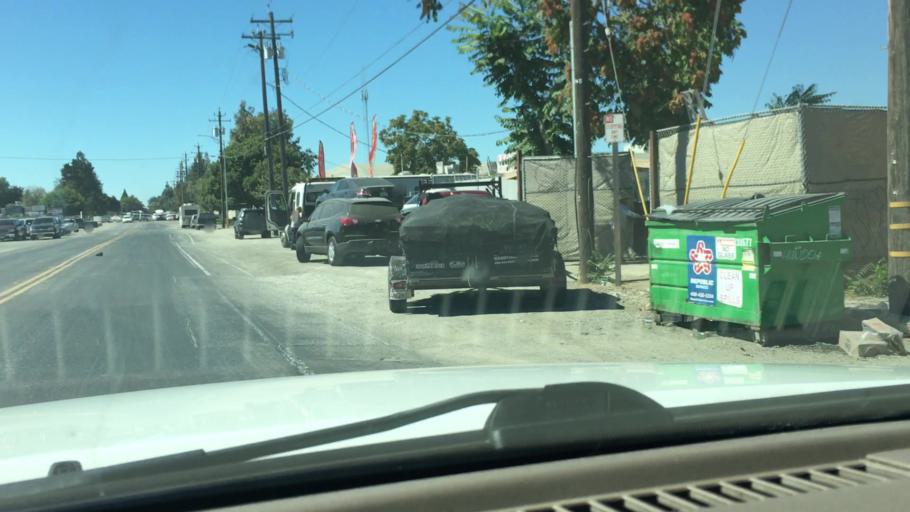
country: US
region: California
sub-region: Santa Clara County
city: San Jose
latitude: 37.3141
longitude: -121.8655
